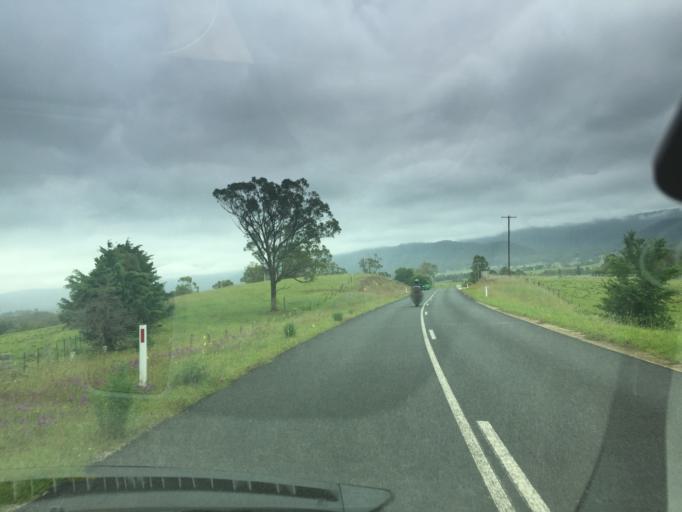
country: AU
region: New South Wales
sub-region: Bega Valley
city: Bega
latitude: -36.6476
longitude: 149.5841
